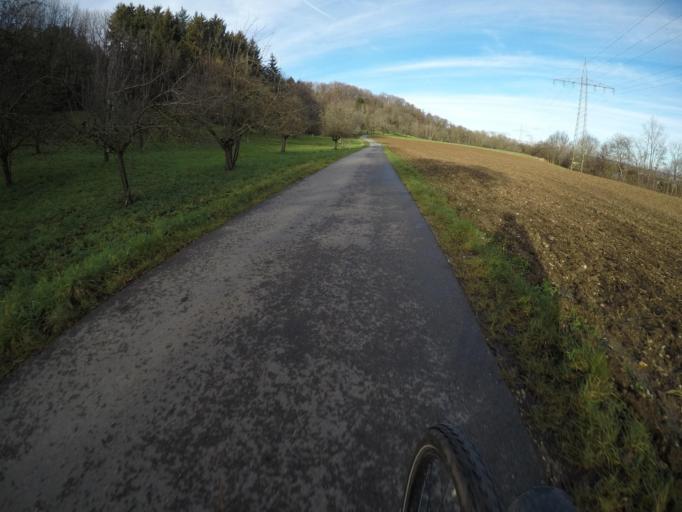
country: DE
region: Baden-Wuerttemberg
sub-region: Regierungsbezirk Stuttgart
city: Owen
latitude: 48.5970
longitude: 9.4435
